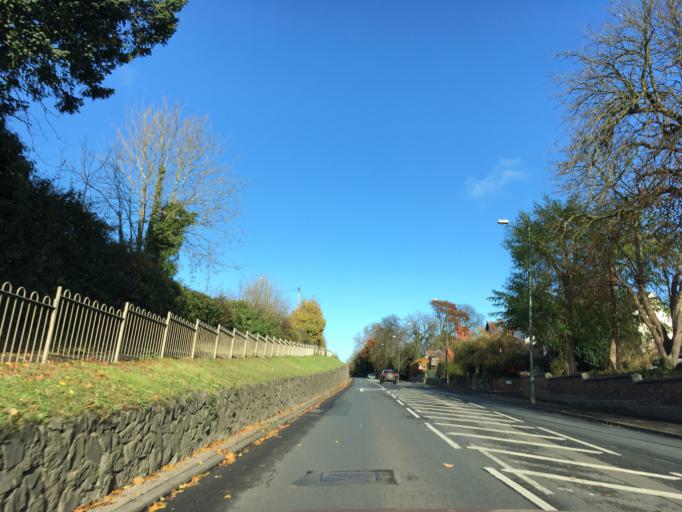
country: GB
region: England
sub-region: Worcestershire
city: Evesham
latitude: 52.1002
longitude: -1.9451
